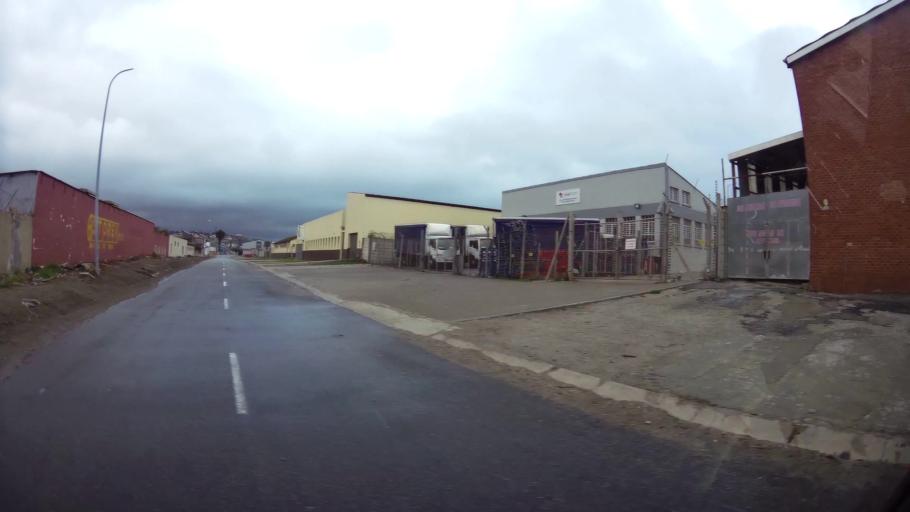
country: ZA
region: Eastern Cape
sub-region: Nelson Mandela Bay Metropolitan Municipality
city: Port Elizabeth
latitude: -33.9267
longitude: 25.5938
